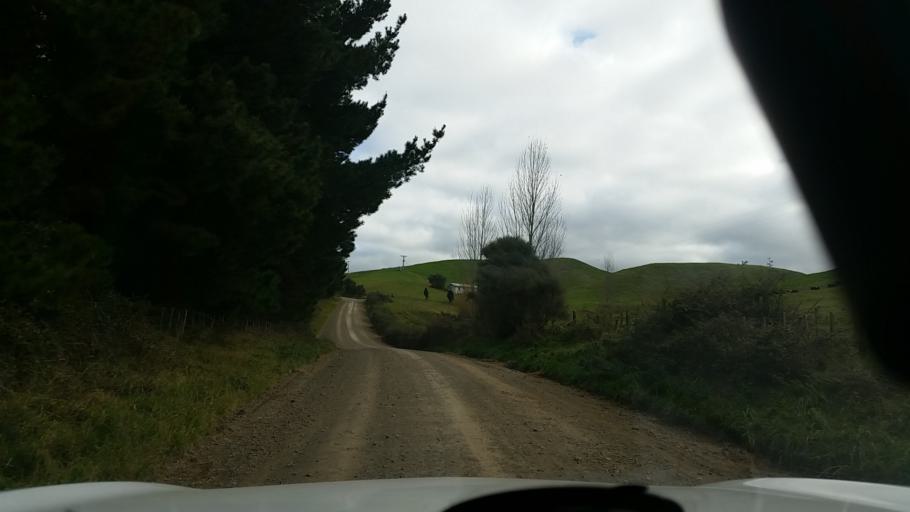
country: NZ
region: Hawke's Bay
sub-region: Napier City
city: Napier
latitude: -39.1781
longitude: 176.8600
